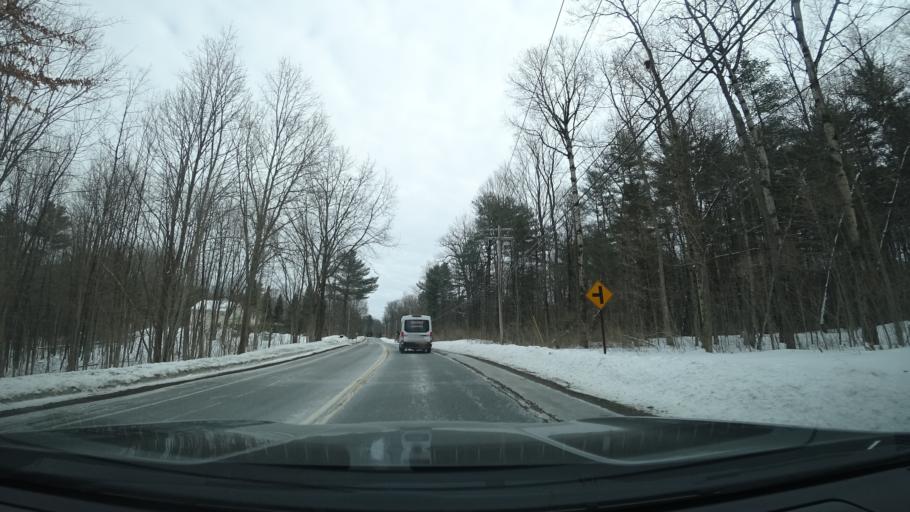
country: US
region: New York
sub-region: Washington County
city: Fort Edward
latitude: 43.2609
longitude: -73.6039
